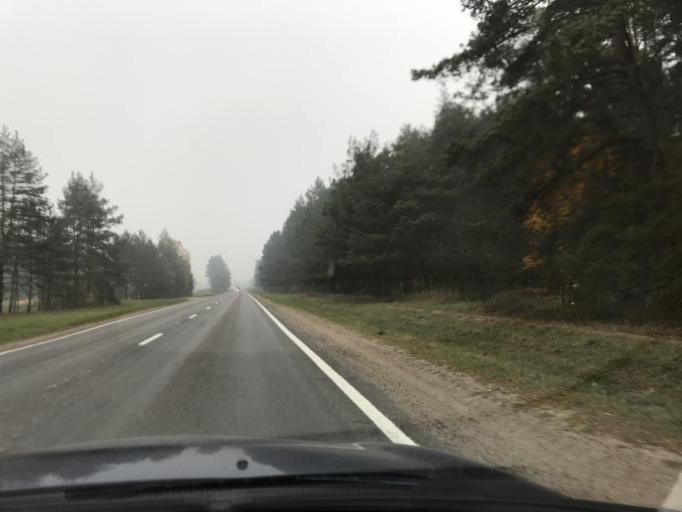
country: BY
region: Grodnenskaya
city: Hrodna
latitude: 53.7932
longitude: 23.8549
